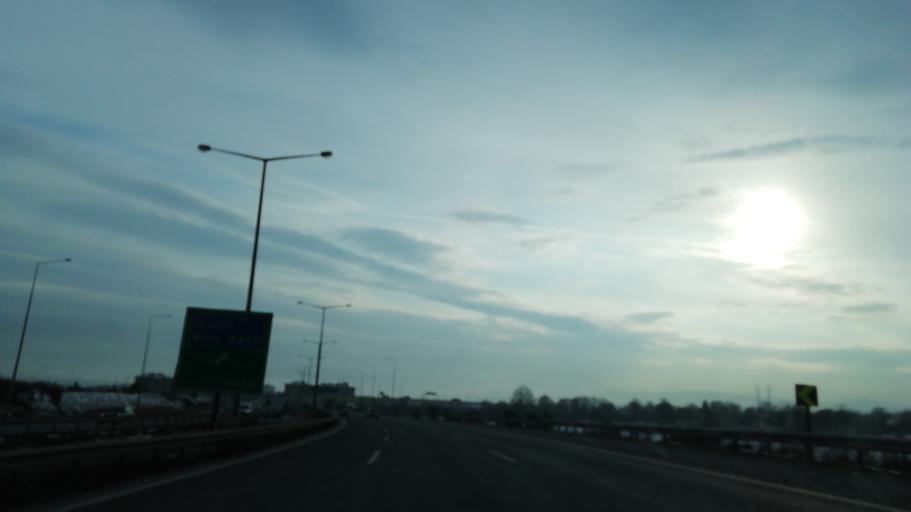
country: TR
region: Bolu
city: Bolu
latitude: 40.7480
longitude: 31.5614
